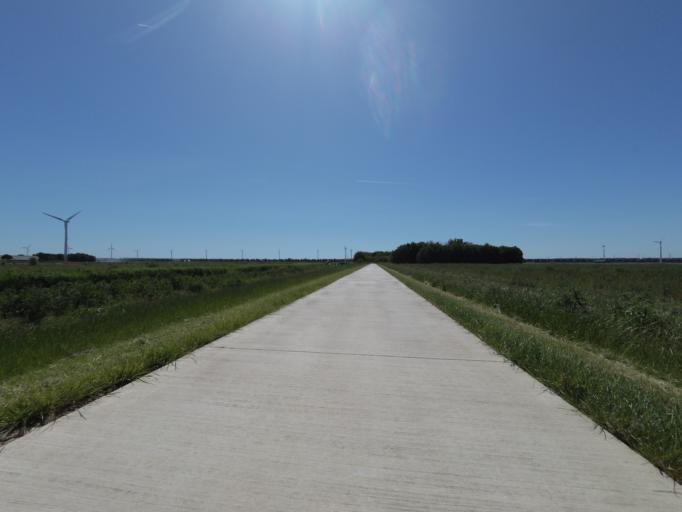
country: NL
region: Utrecht
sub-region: Gemeente Bunschoten
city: Spakenburg
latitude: 52.3440
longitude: 5.4071
